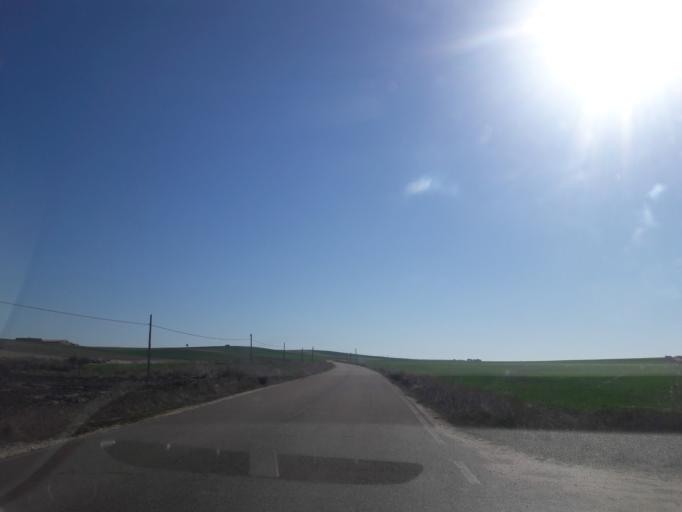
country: ES
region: Castille and Leon
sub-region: Provincia de Salamanca
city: Tordillos
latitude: 40.8511
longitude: -5.3355
